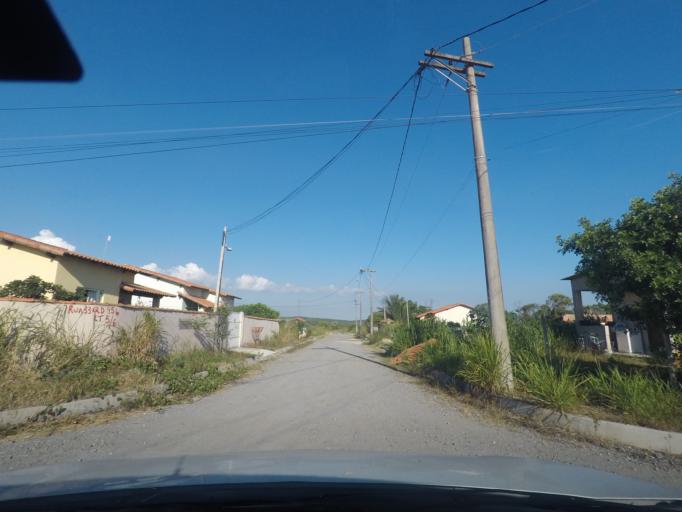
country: BR
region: Rio de Janeiro
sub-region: Marica
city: Marica
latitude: -22.9619
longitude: -42.9254
